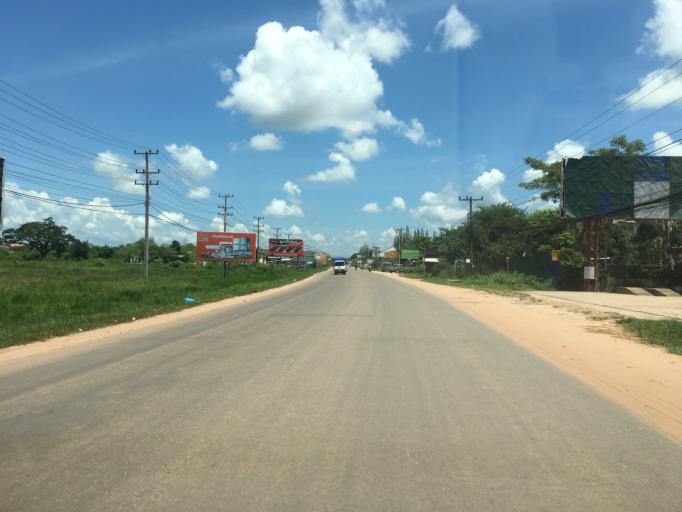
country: LA
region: Vientiane
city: Vientiane
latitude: 18.0327
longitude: 102.5480
